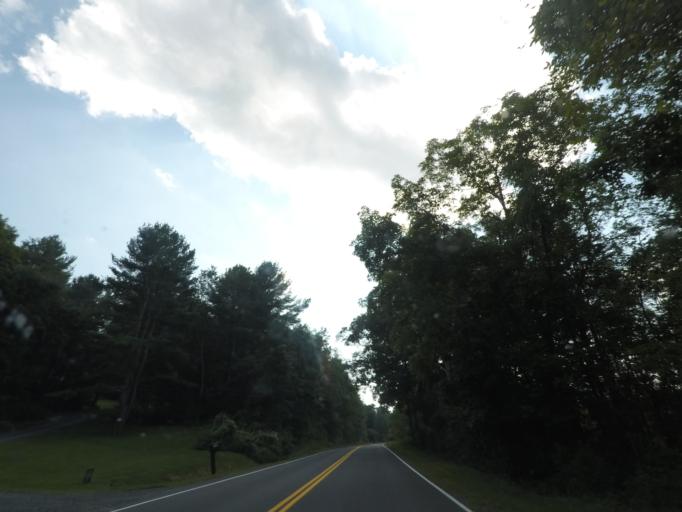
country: US
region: New York
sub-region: Rensselaer County
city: Poestenkill
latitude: 42.7747
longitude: -73.5392
